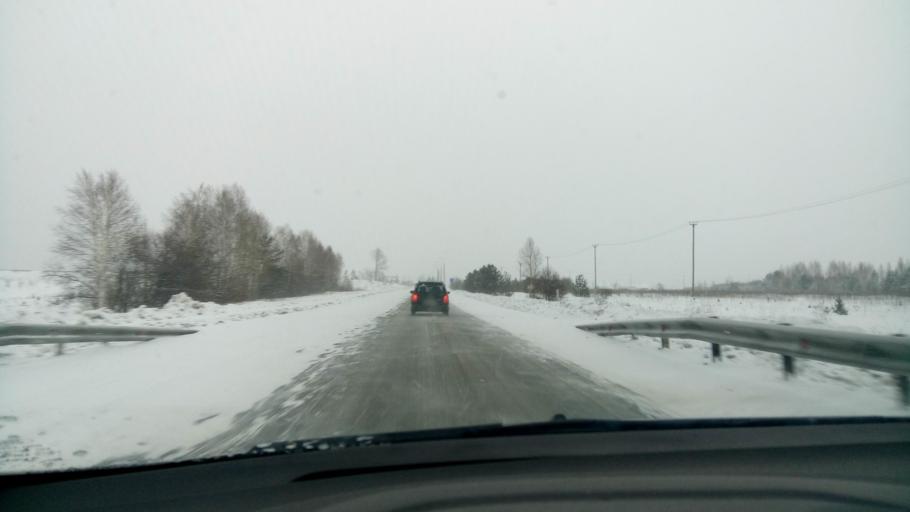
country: RU
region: Sverdlovsk
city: Verkhneye Dubrovo
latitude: 56.7360
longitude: 61.1047
